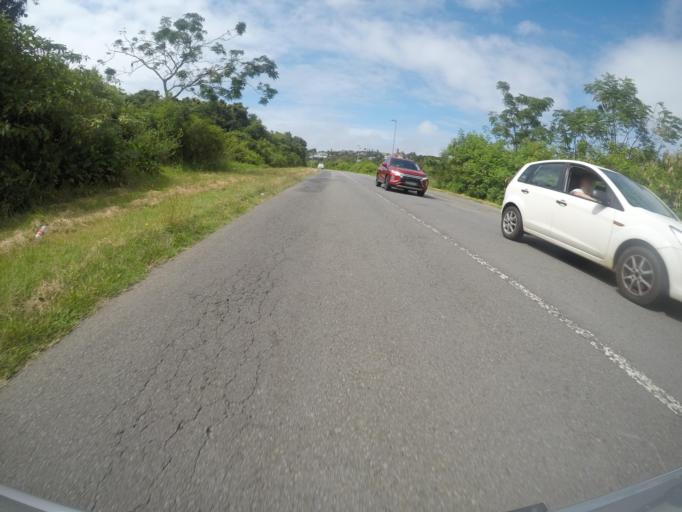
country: ZA
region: Eastern Cape
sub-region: Buffalo City Metropolitan Municipality
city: East London
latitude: -32.9768
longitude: 27.9333
